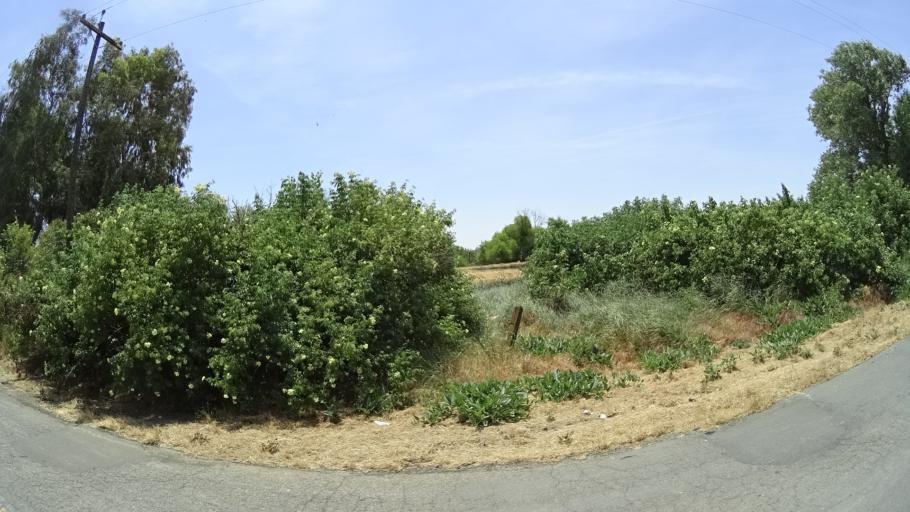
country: US
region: California
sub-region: Fresno County
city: Riverdale
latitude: 36.3875
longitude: -119.8772
